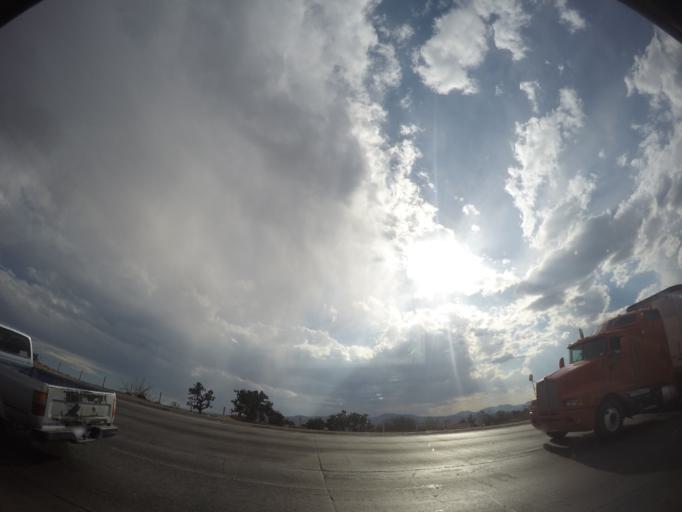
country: MX
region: Mexico
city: San Francisco Soyaniquilpan
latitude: 20.0255
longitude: -99.5341
